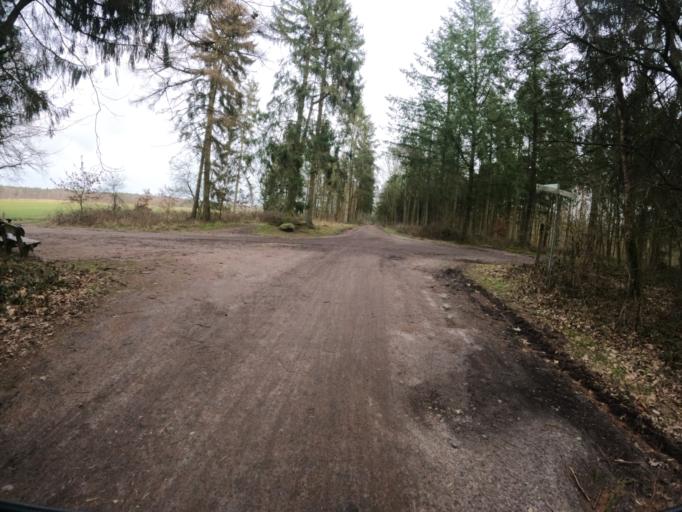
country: DE
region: Schleswig-Holstein
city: Appen
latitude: 53.6129
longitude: 9.7534
